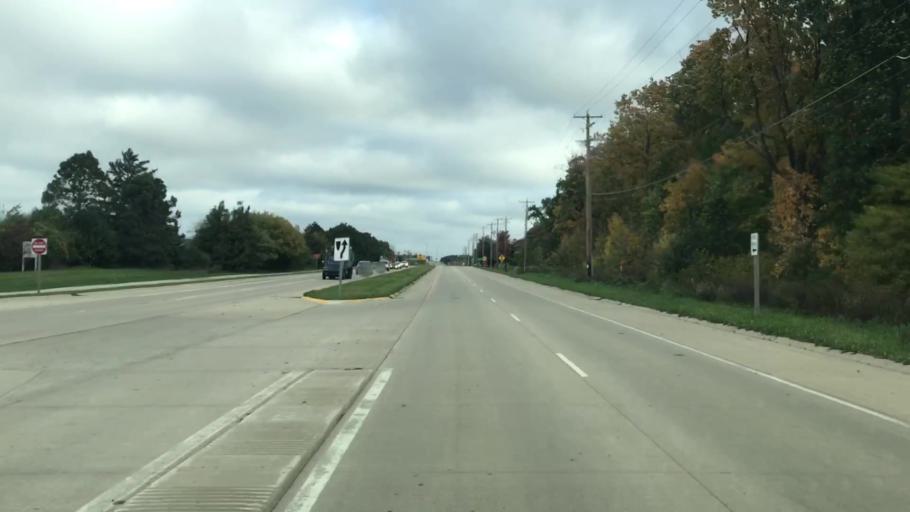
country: US
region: Wisconsin
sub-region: Waukesha County
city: Pewaukee
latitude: 43.0570
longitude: -88.2252
